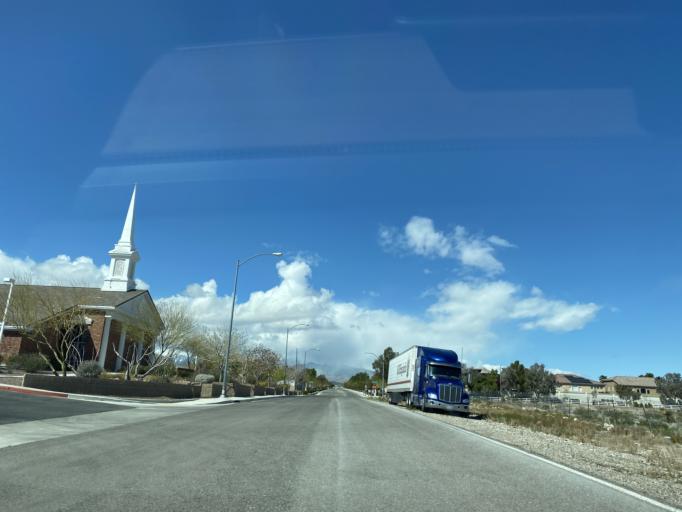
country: US
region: Nevada
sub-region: Clark County
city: North Las Vegas
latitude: 36.3213
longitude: -115.2861
